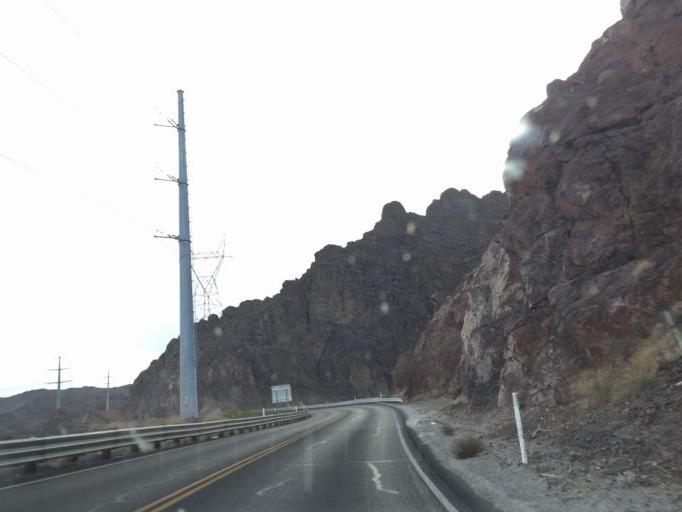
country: US
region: Nevada
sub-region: Clark County
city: Boulder City
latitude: 36.0130
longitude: -114.7608
